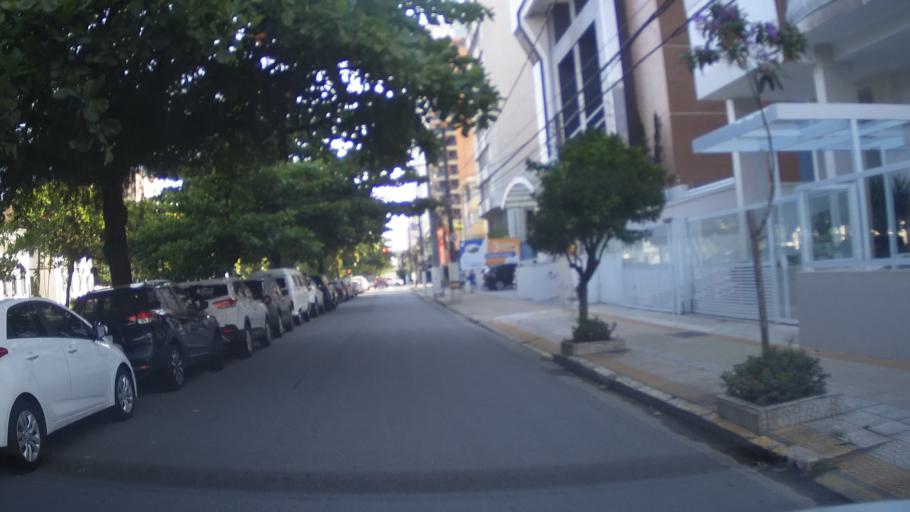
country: BR
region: Sao Paulo
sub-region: Santos
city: Santos
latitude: -23.9806
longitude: -46.3051
